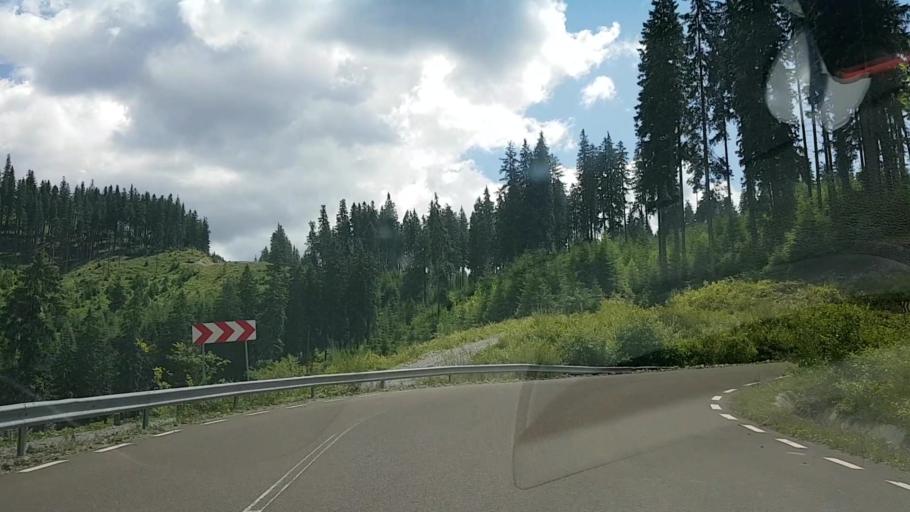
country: RO
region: Suceava
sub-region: Comuna Sadova
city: Sadova
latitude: 47.4597
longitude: 25.5180
